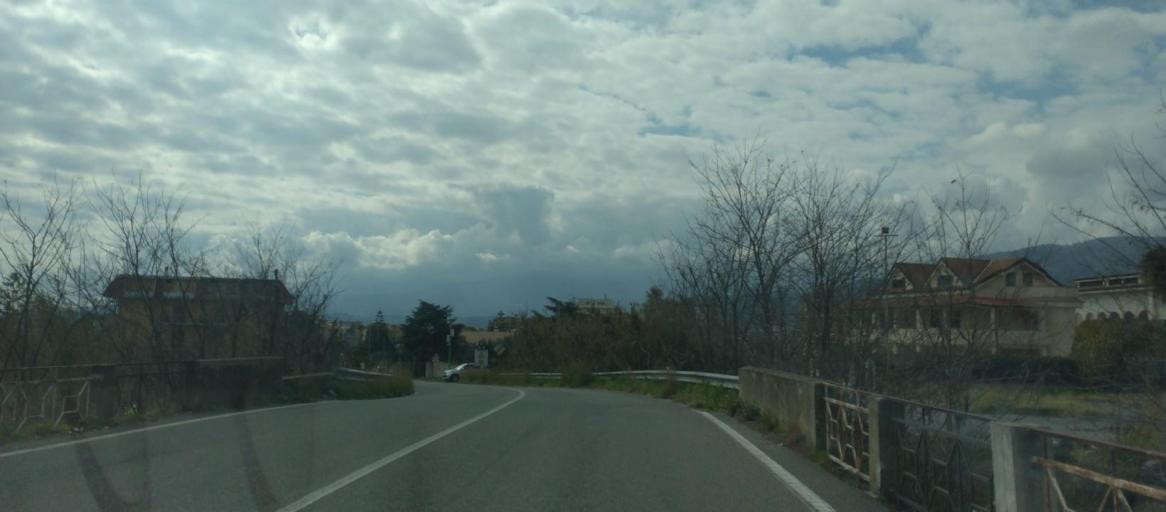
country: IT
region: Calabria
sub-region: Provincia di Catanzaro
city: Montepaone Lido
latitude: 38.7336
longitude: 16.5451
